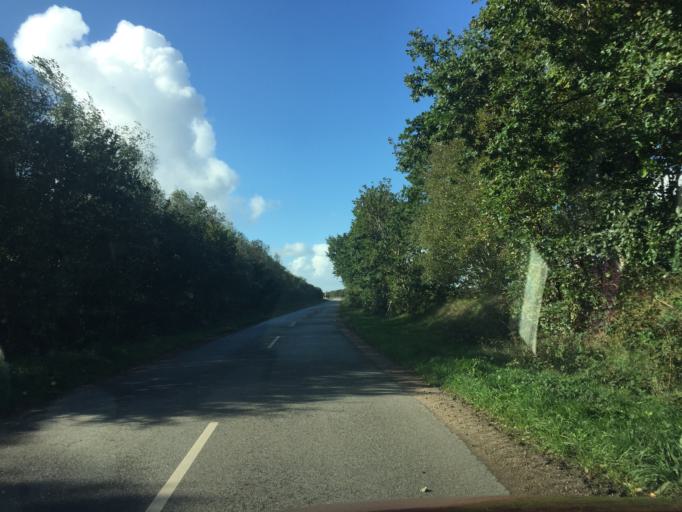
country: DK
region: South Denmark
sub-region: Tonder Kommune
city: Sherrebek
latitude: 55.0825
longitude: 8.7715
